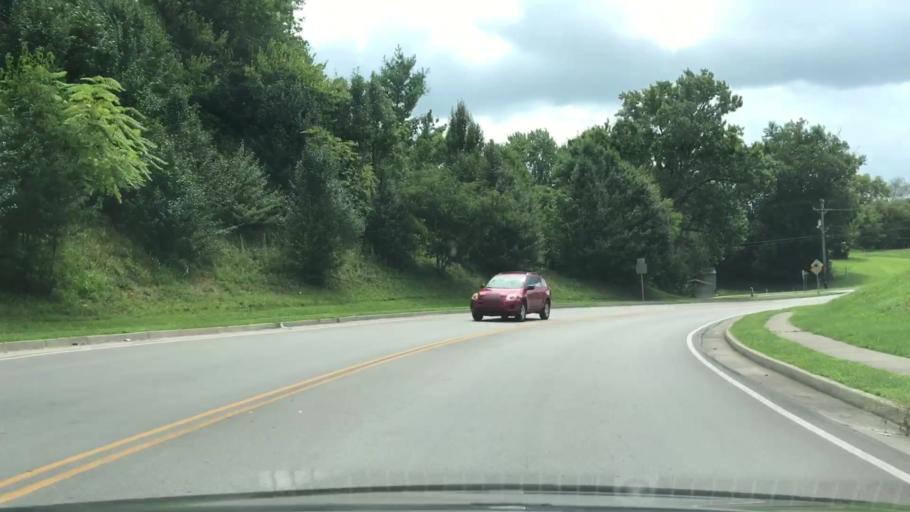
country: US
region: Kentucky
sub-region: Pulaski County
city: Somerset
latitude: 37.0801
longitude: -84.6080
